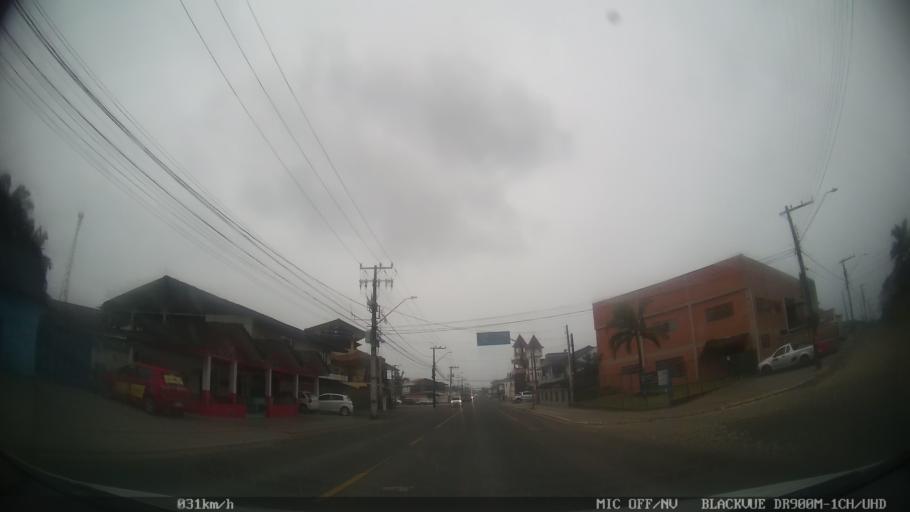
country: BR
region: Santa Catarina
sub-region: Joinville
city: Joinville
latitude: -26.2844
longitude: -48.8086
